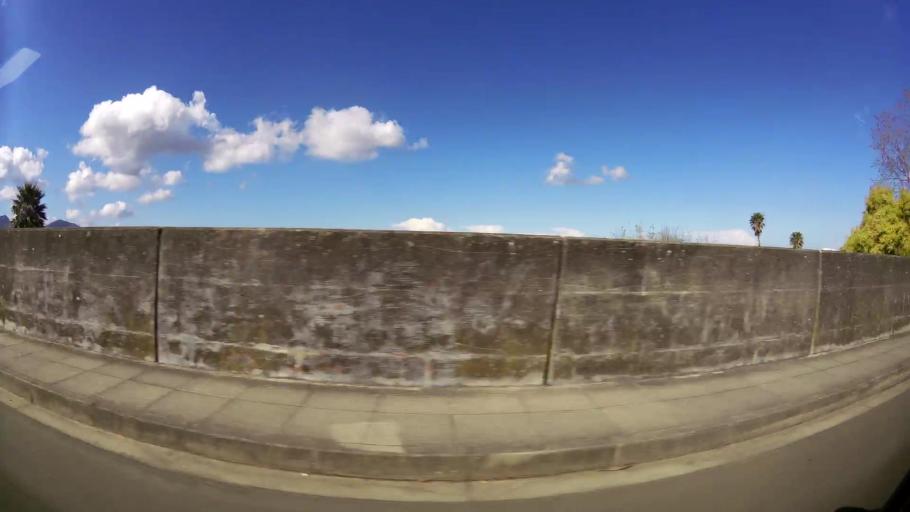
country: ZA
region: Western Cape
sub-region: Eden District Municipality
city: George
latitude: -33.9507
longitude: 22.4655
